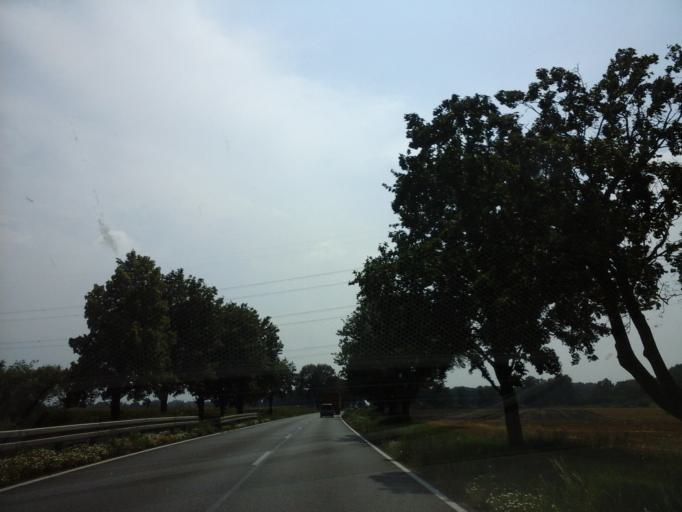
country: PL
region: Lower Silesian Voivodeship
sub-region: Powiat wroclawski
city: Zorawina
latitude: 50.9508
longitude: 17.0709
